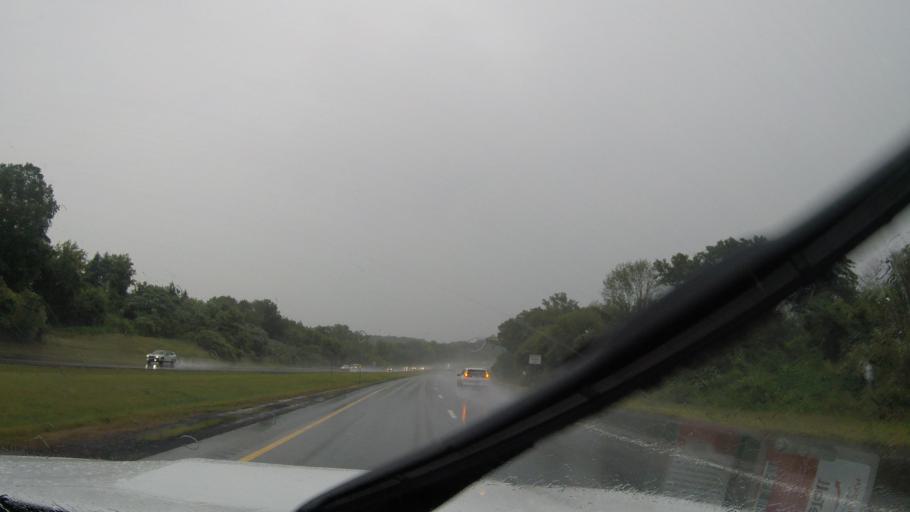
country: US
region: New York
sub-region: Ontario County
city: Geneva
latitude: 42.9589
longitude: -76.9515
